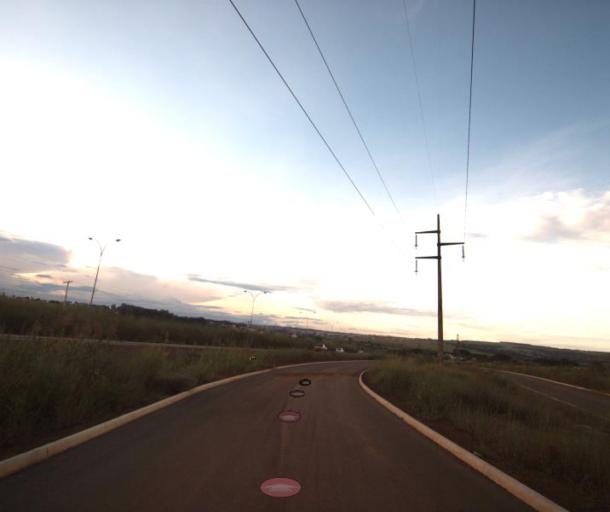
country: BR
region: Goias
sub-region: Anapolis
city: Anapolis
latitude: -16.3153
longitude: -48.9214
